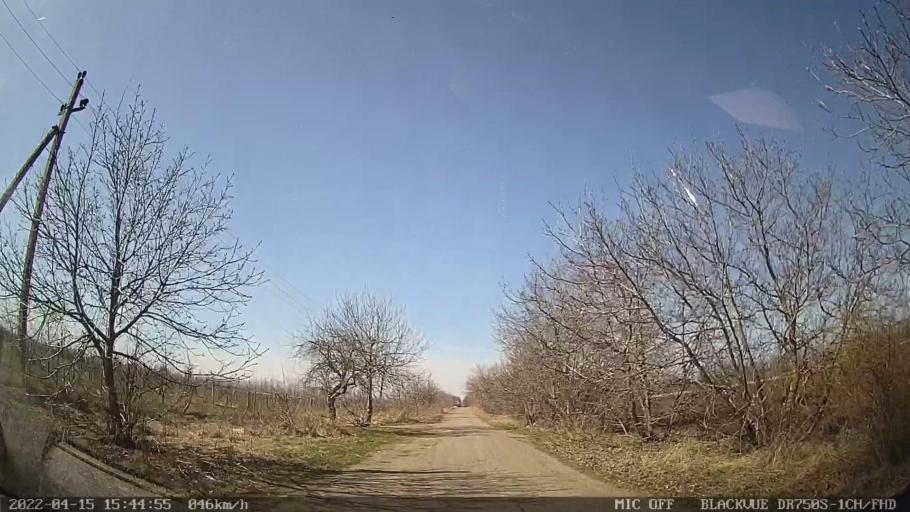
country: MD
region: Raionul Ocnita
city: Otaci
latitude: 48.3730
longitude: 27.9206
